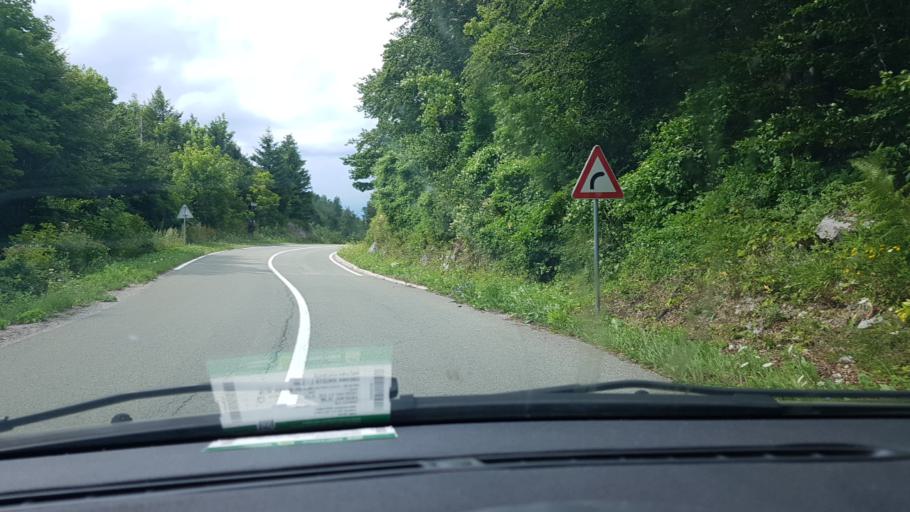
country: HR
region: Primorsko-Goranska
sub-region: Grad Delnice
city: Delnice
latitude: 45.3404
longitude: 14.7520
